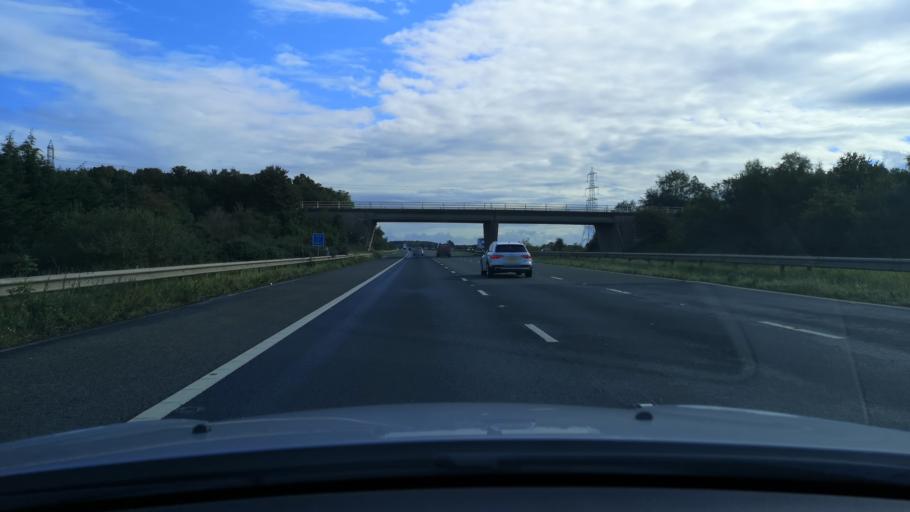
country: GB
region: England
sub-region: East Riding of Yorkshire
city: Pollington
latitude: 53.6812
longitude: -1.0576
